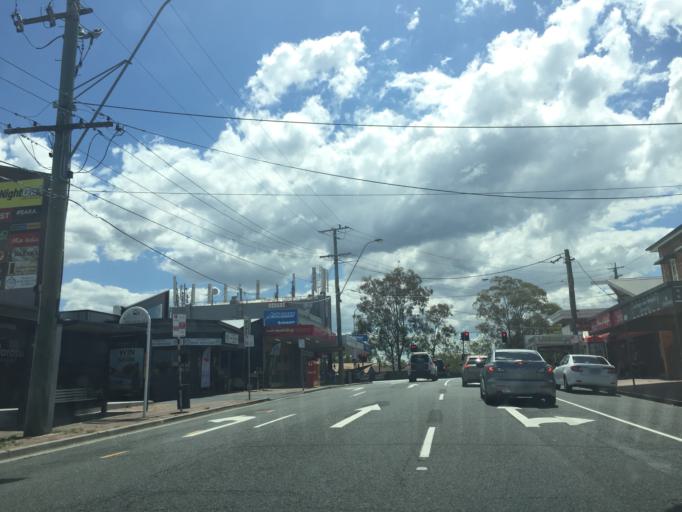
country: AU
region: Queensland
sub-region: Brisbane
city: Milton
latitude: -27.4492
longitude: 152.9782
